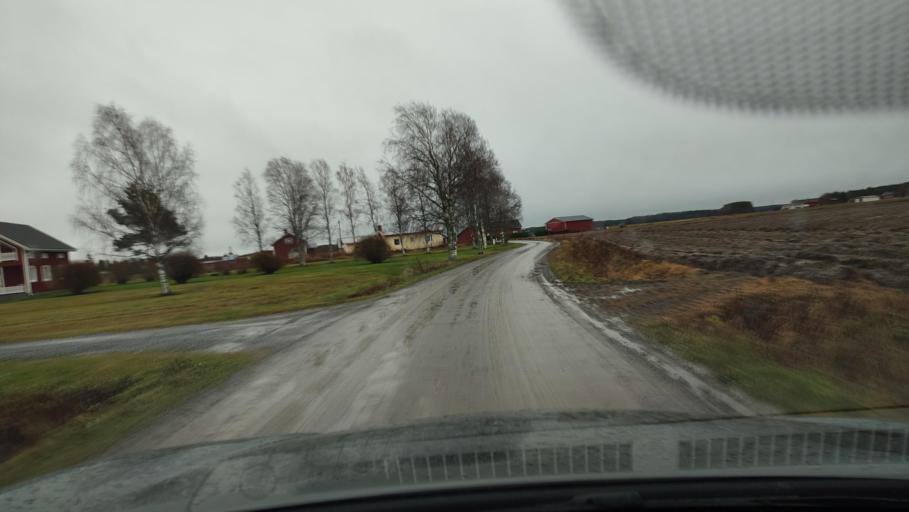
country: FI
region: Southern Ostrobothnia
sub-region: Suupohja
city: Karijoki
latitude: 62.2445
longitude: 21.5500
